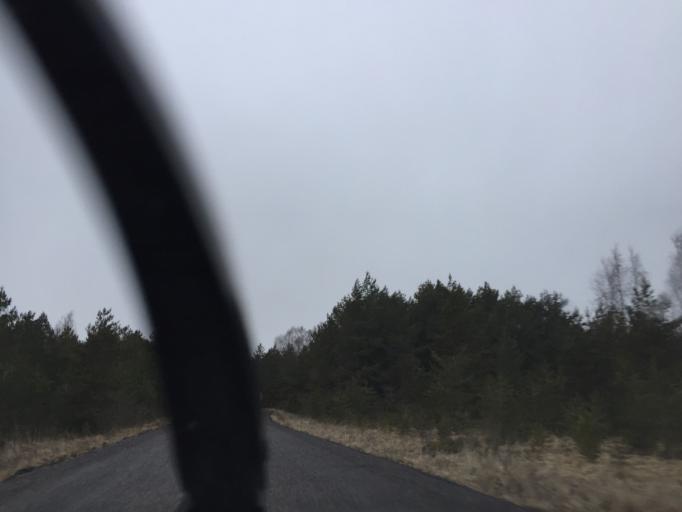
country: EE
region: Laeaene
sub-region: Ridala Parish
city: Uuemoisa
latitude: 58.6728
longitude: 23.5602
